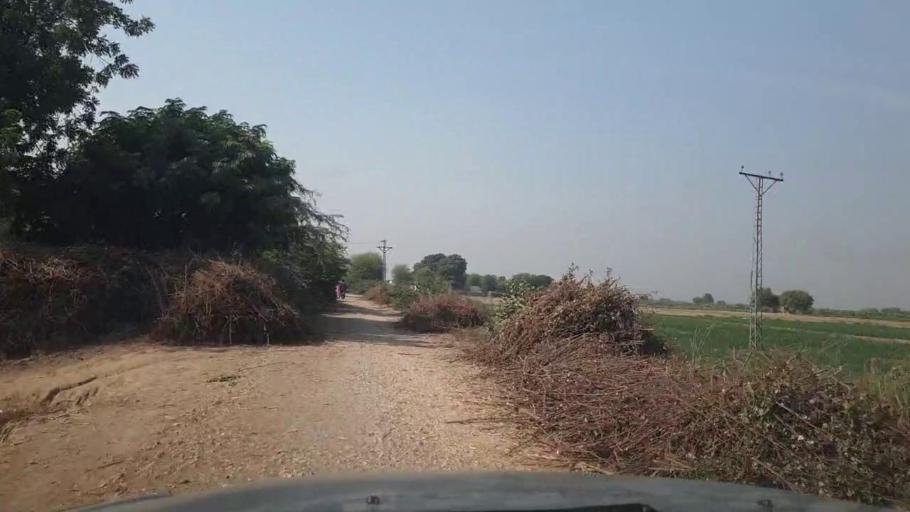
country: PK
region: Sindh
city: Bhit Shah
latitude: 25.7383
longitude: 68.5035
